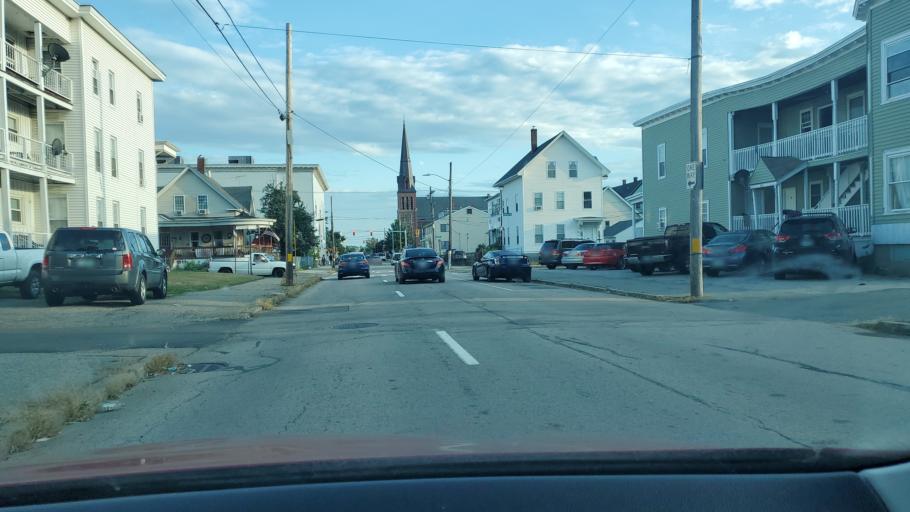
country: US
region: New Hampshire
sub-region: Hillsborough County
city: Manchester
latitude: 42.9885
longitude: -71.4553
